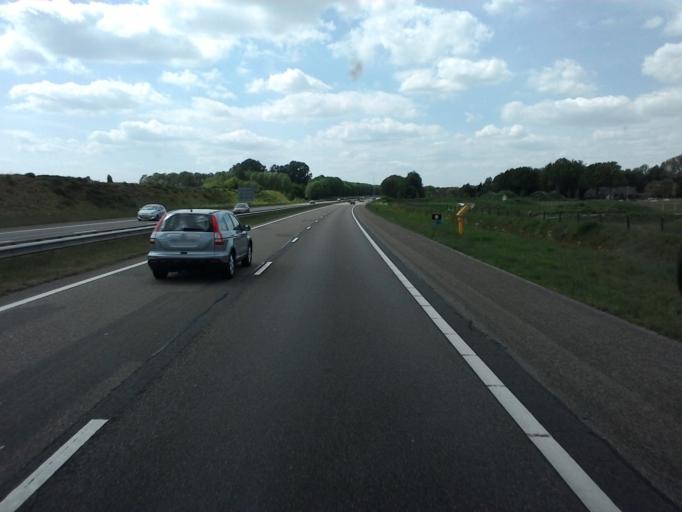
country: NL
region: North Brabant
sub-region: Gemeente Boxmeer
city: Boxmeer
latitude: 51.6620
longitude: 5.9363
